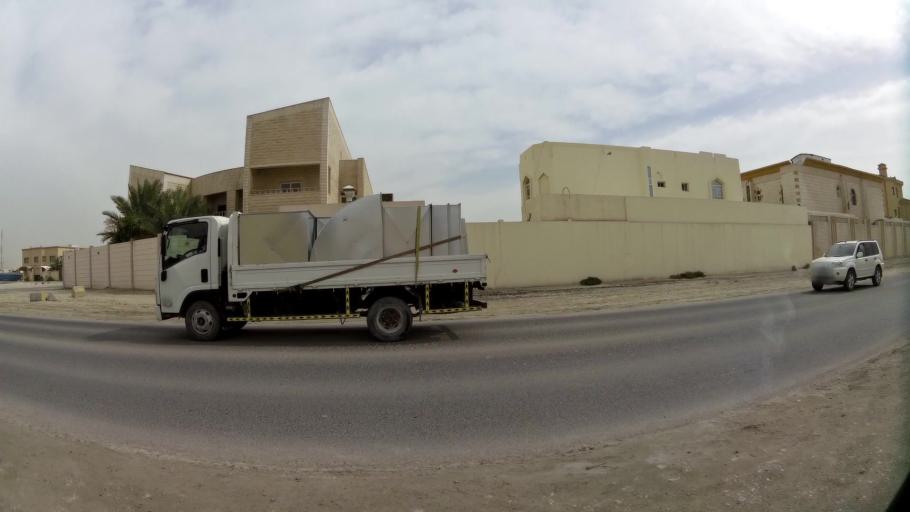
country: QA
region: Baladiyat ad Dawhah
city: Doha
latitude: 25.2242
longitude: 51.4881
